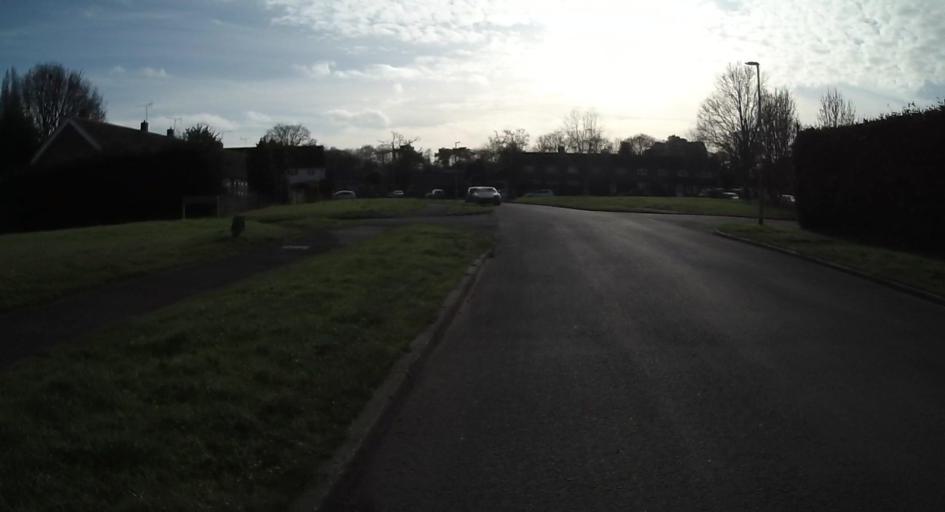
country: GB
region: England
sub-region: Wokingham
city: Wokingham
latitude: 51.4006
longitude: -0.8393
